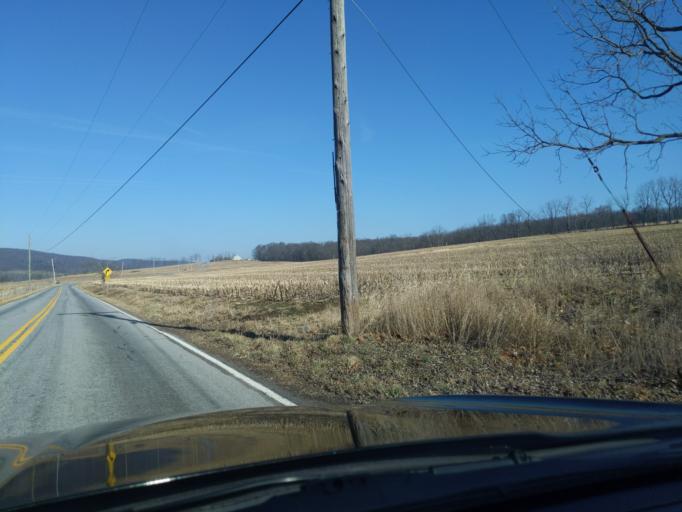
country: US
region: Pennsylvania
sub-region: Blair County
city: Tipton
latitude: 40.6020
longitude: -78.2652
